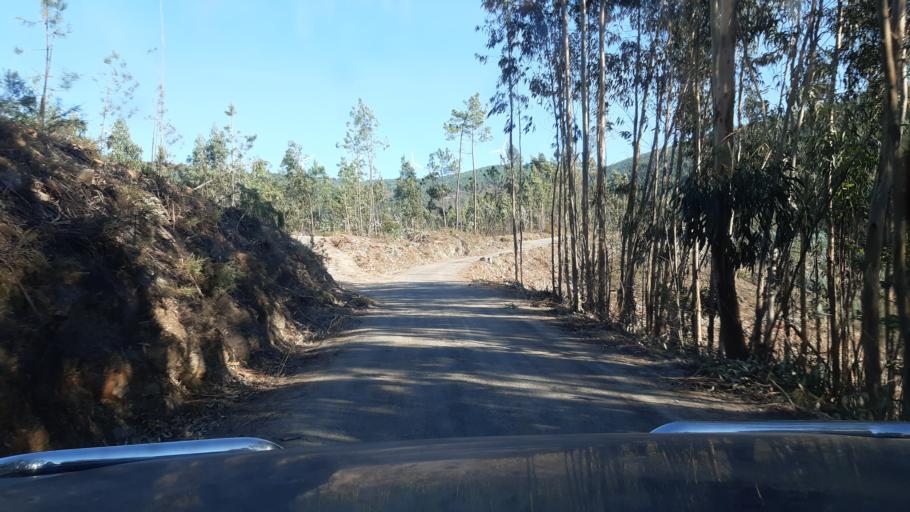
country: PT
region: Viseu
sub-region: Mortagua
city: Mortagua
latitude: 40.5258
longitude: -8.2547
